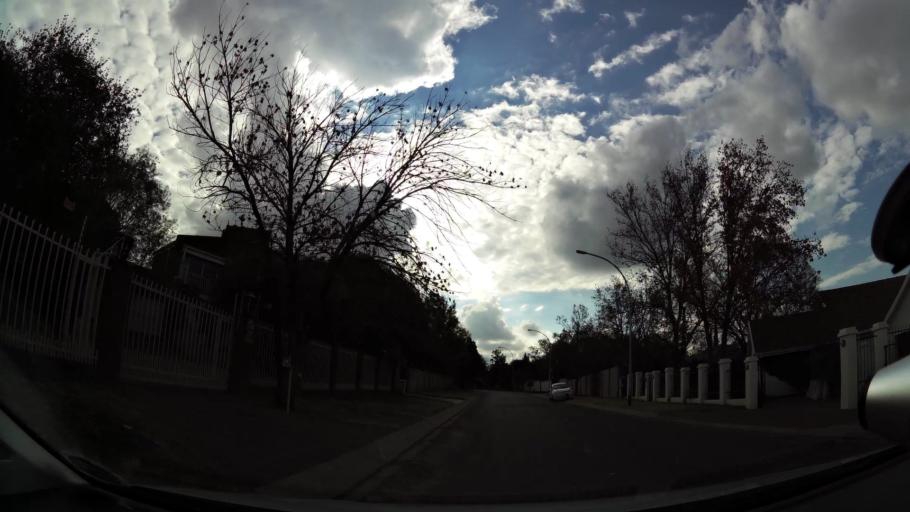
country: ZA
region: Orange Free State
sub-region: Mangaung Metropolitan Municipality
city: Bloemfontein
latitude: -29.0800
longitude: 26.2037
